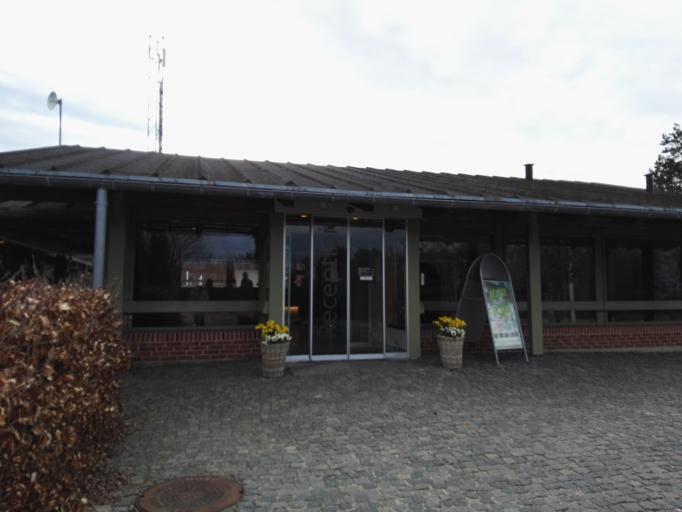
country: DK
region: Capital Region
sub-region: Gribskov Kommune
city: Gilleleje
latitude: 56.1231
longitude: 12.2672
